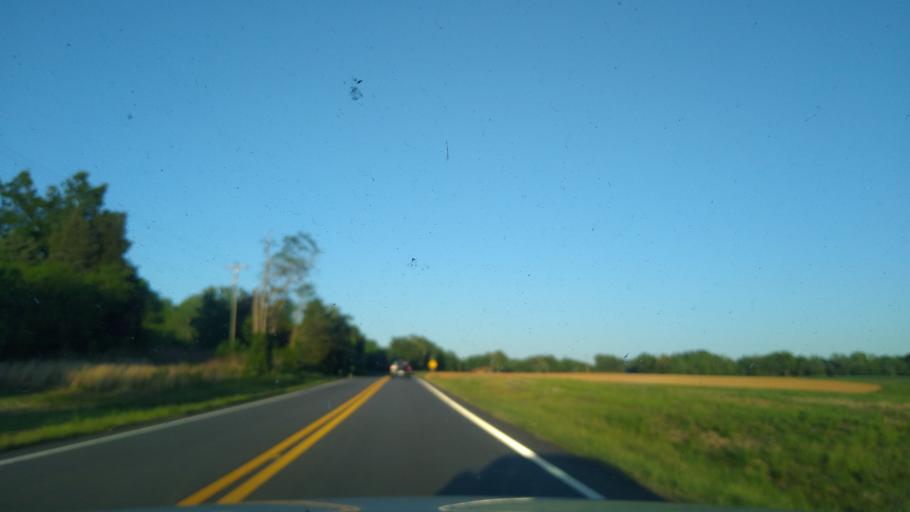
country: US
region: North Carolina
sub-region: Caswell County
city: Yanceyville
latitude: 36.3864
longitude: -79.4916
